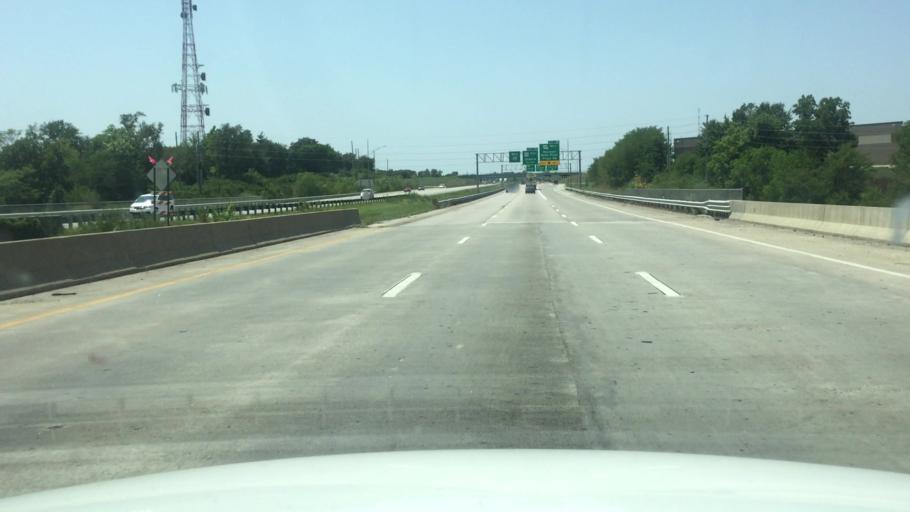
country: US
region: Missouri
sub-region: Jackson County
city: Lees Summit
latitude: 38.9416
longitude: -94.3902
